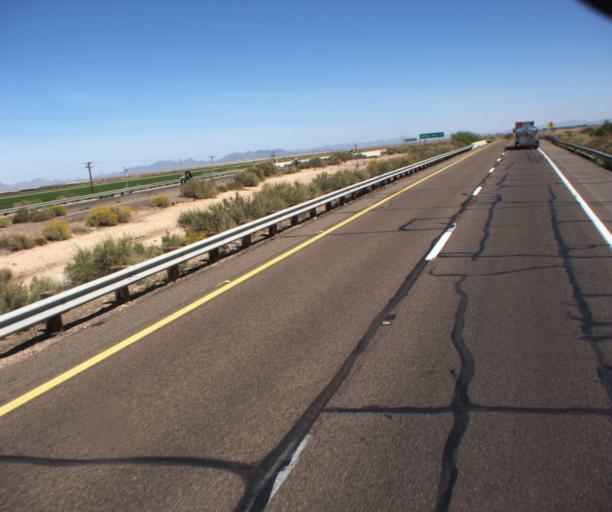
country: US
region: Arizona
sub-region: Maricopa County
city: Gila Bend
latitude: 32.9111
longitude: -112.9606
